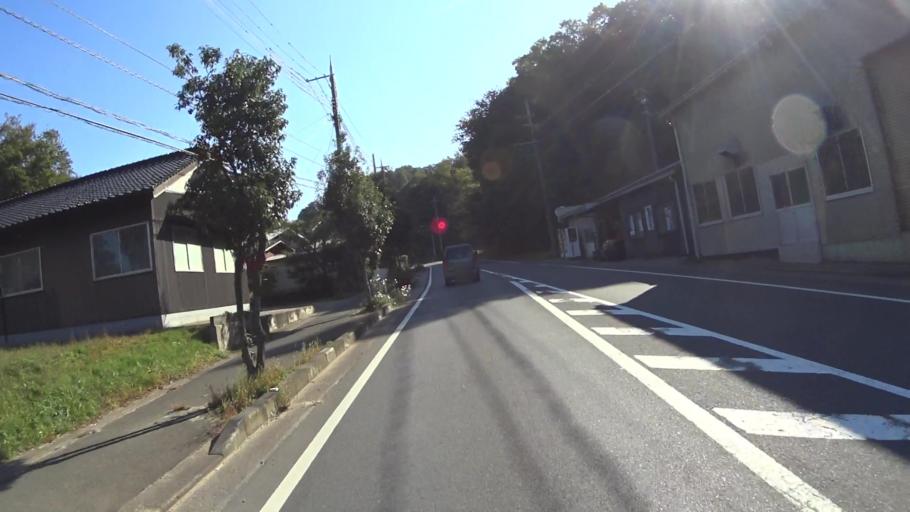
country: JP
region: Kyoto
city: Miyazu
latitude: 35.6357
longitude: 135.0540
